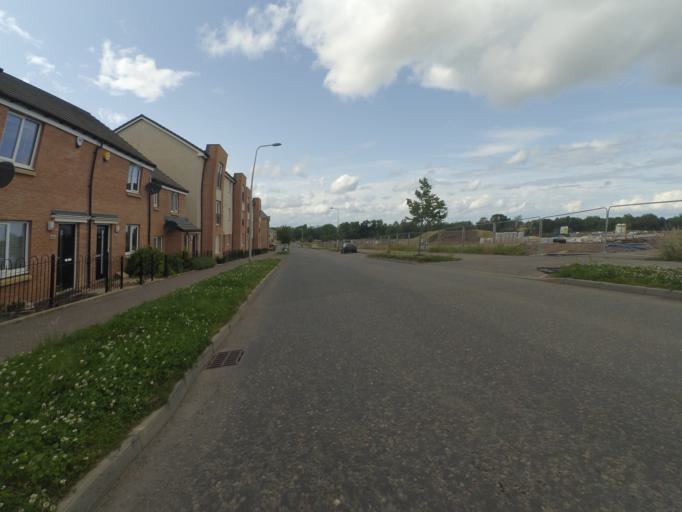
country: GB
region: Scotland
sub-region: West Lothian
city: Seafield
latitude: 55.9245
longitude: -3.1185
